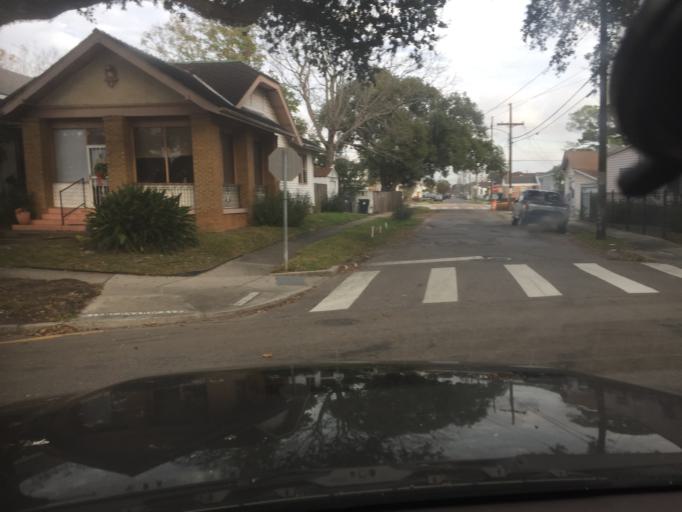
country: US
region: Louisiana
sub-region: Orleans Parish
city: New Orleans
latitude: 29.9869
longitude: -90.0738
